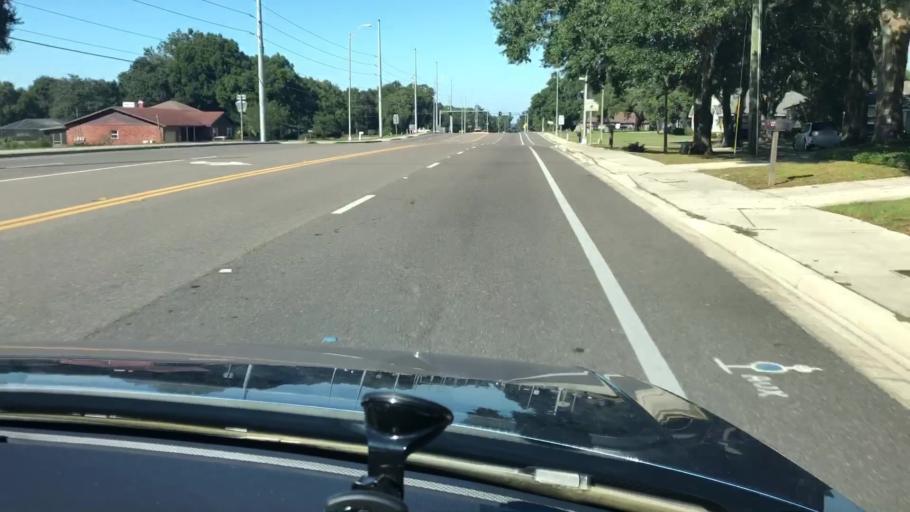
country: US
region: Florida
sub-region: Polk County
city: Kathleen
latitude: 28.1329
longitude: -82.0233
